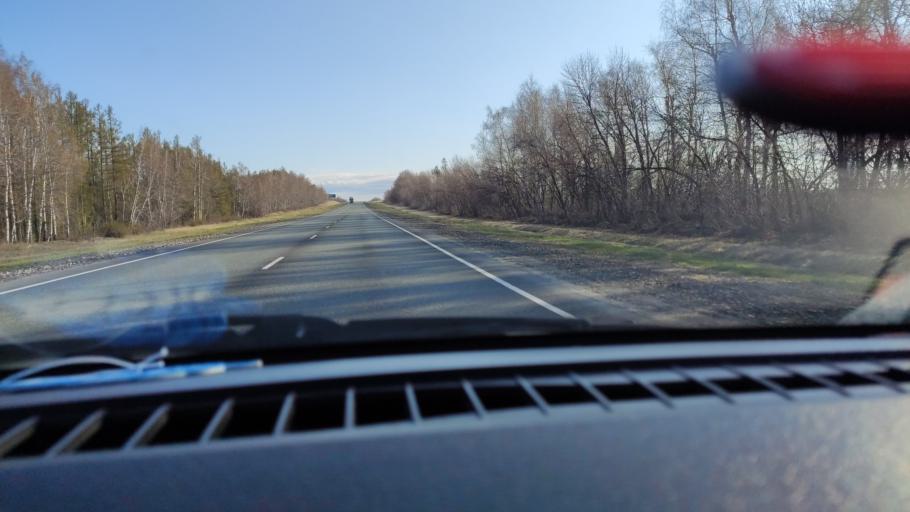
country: RU
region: Saratov
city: Khvalynsk
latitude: 52.5833
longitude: 48.1199
